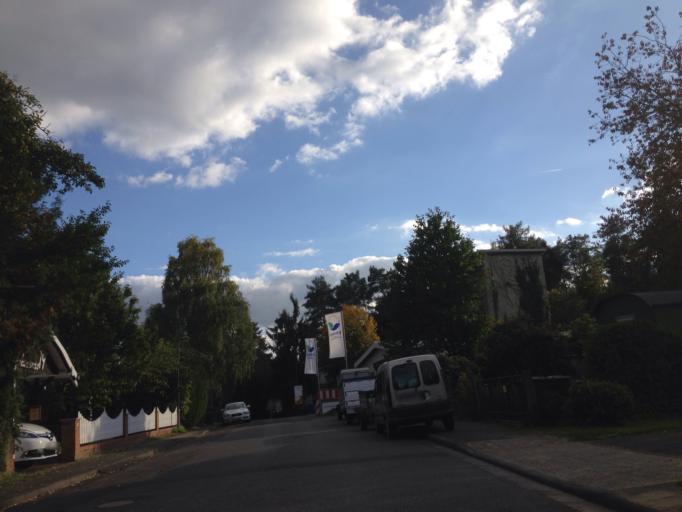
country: DE
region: Hesse
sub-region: Regierungsbezirk Giessen
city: Giessen
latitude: 50.5648
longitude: 8.6756
